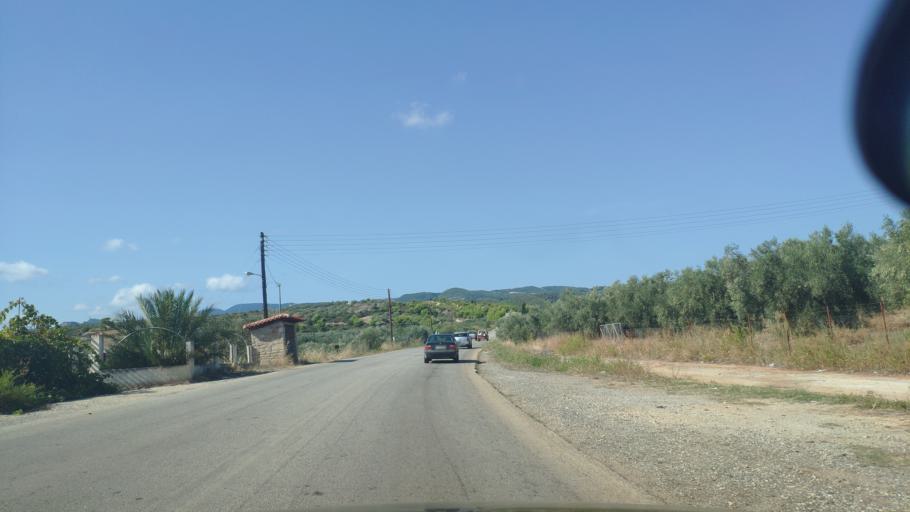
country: GR
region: Peloponnese
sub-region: Nomos Korinthias
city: Moulki
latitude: 37.9904
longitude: 22.6970
